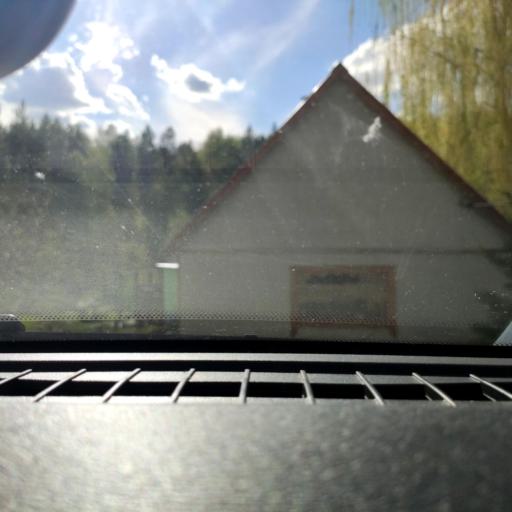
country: RU
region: Samara
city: Zhigulevsk
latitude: 53.3693
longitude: 49.5084
